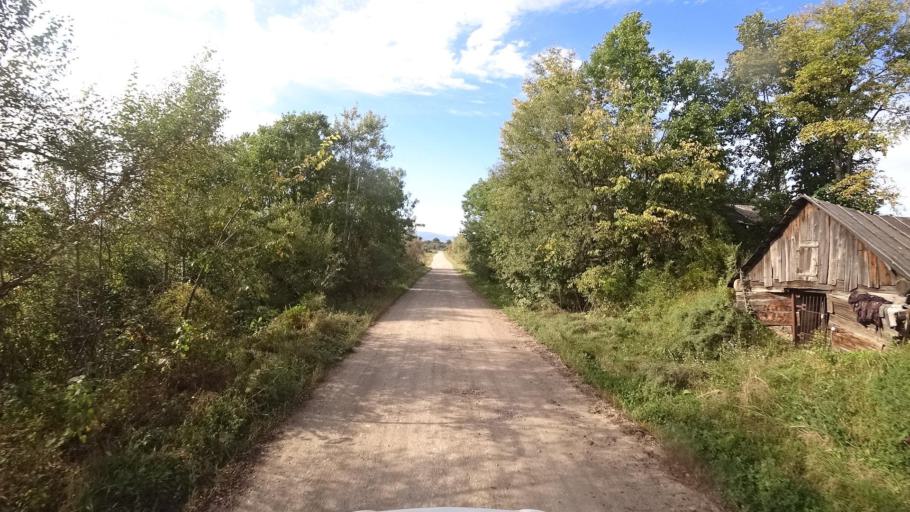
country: RU
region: Primorskiy
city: Dostoyevka
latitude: 44.3077
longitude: 133.4658
